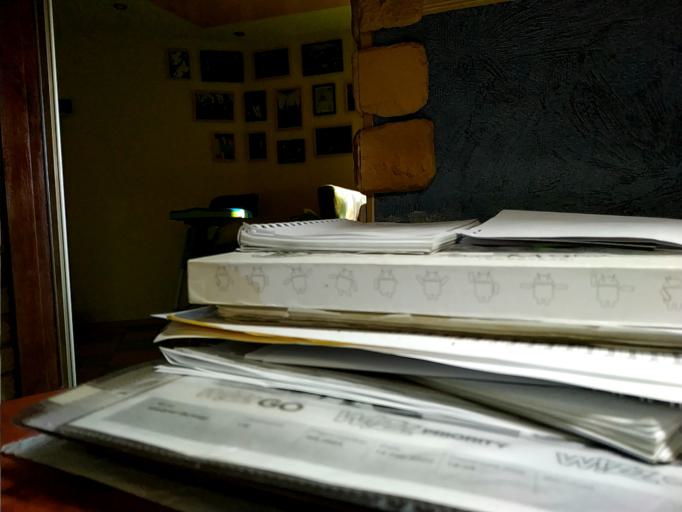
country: RU
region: Novgorod
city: Kholm
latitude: 57.0897
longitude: 31.5171
